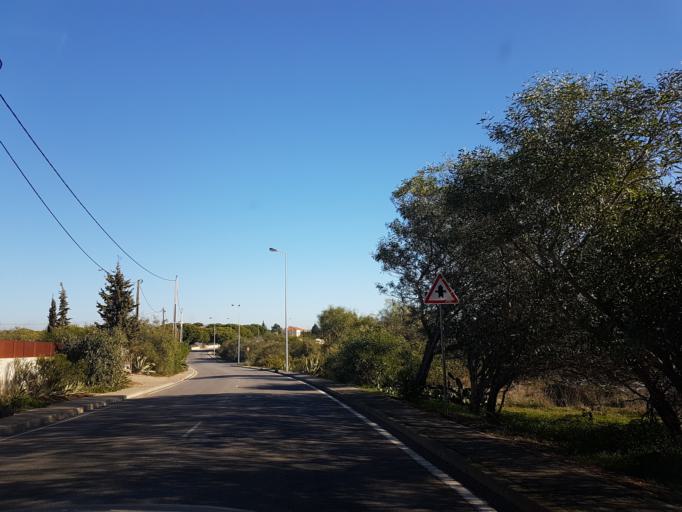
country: PT
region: Faro
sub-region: Lagoa
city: Carvoeiro
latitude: 37.1040
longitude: -8.4392
